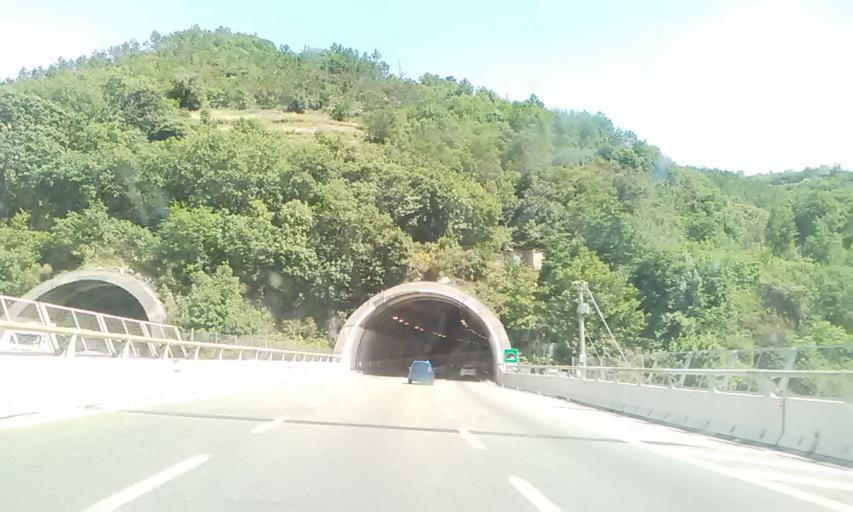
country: IT
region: Liguria
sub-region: Provincia di Genova
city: Mele
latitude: 44.4484
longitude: 8.7154
